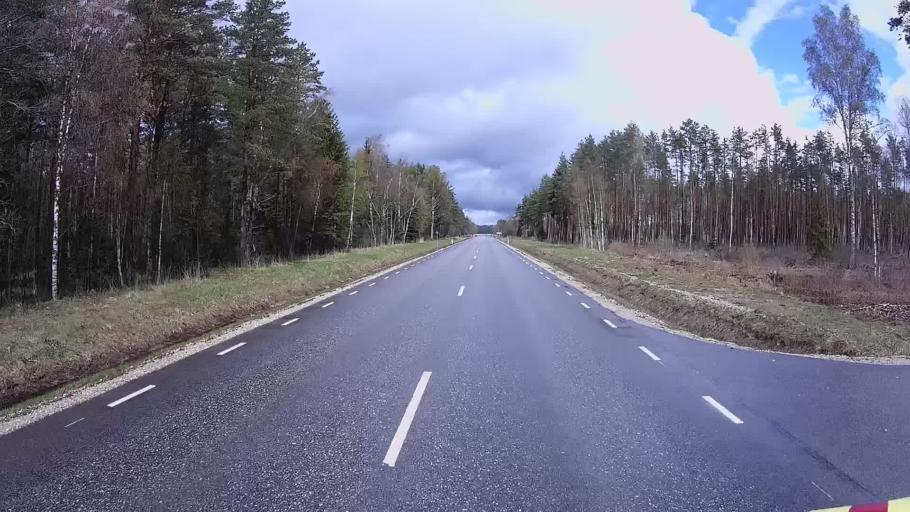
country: EE
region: Hiiumaa
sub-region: Kaerdla linn
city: Kardla
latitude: 58.8662
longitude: 22.7845
